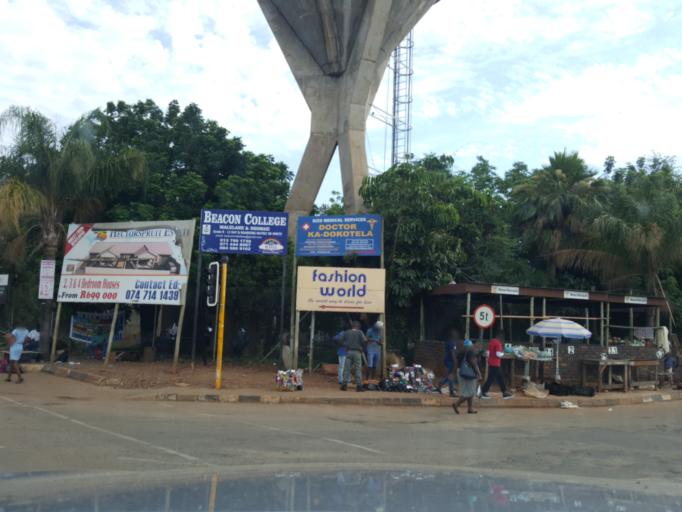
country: SZ
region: Hhohho
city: Ntfonjeni
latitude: -25.4982
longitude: 31.5085
